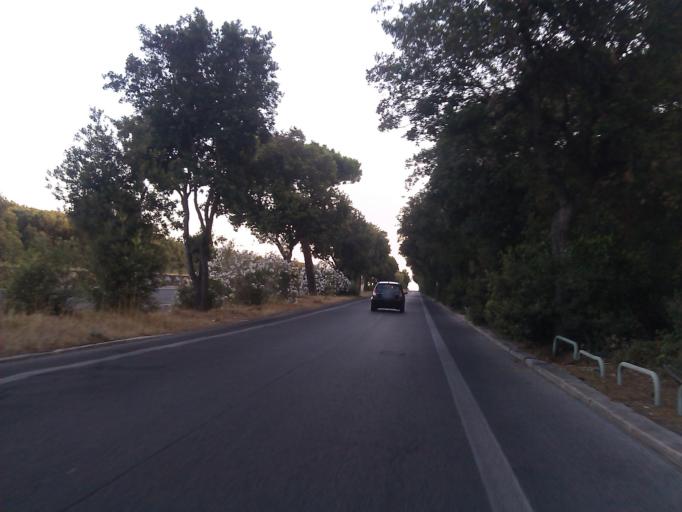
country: IT
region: Latium
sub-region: Citta metropolitana di Roma Capitale
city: Acilia-Castel Fusano-Ostia Antica
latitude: 41.7188
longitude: 12.3224
